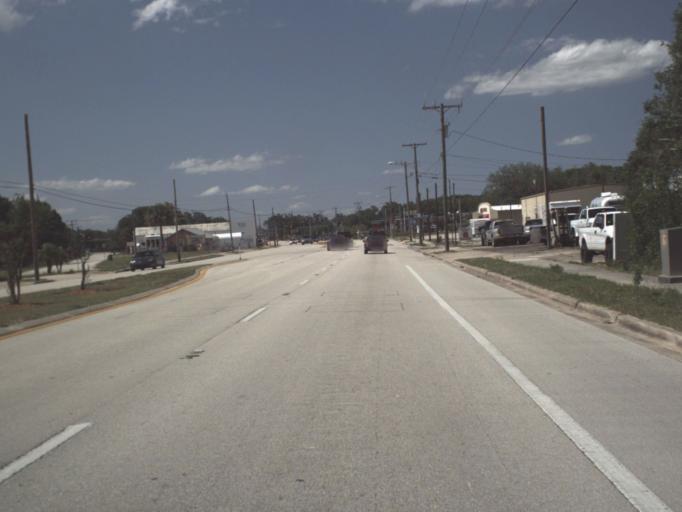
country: US
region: Florida
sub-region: Brevard County
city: Mims
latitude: 28.6621
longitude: -80.8436
